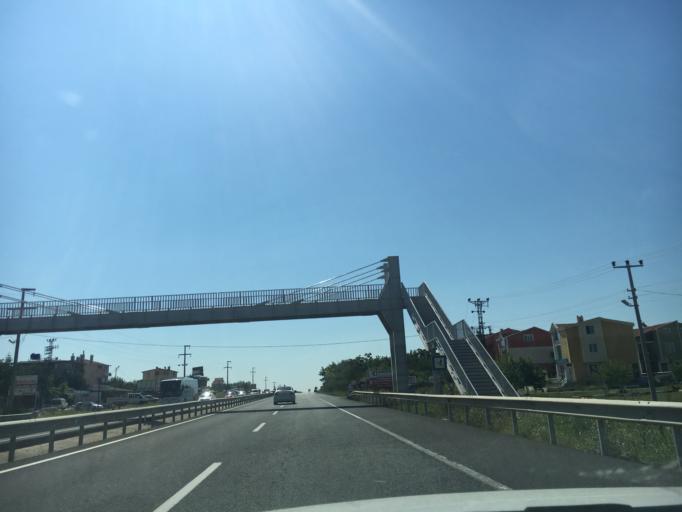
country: TR
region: Tekirdag
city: Marmara Ereglisi
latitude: 40.9770
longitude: 27.8724
